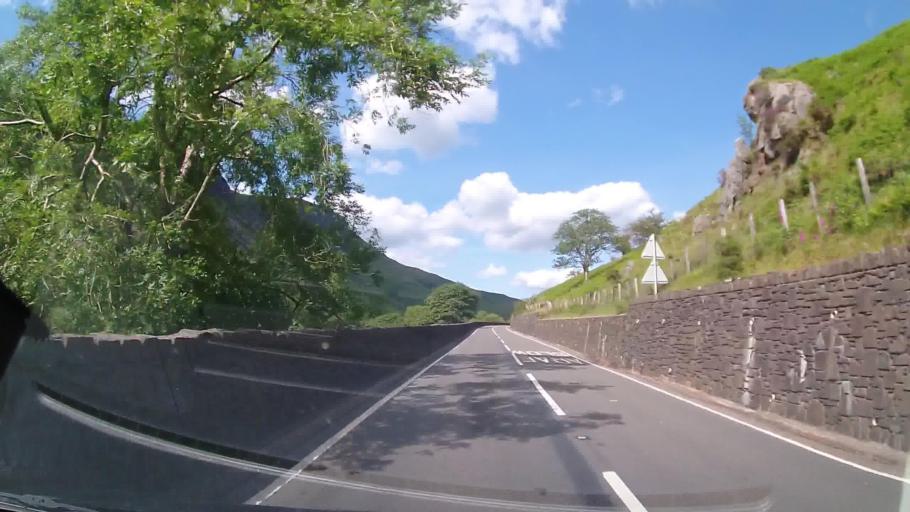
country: GB
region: Wales
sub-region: Gwynedd
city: Corris
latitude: 52.6907
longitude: -3.8666
